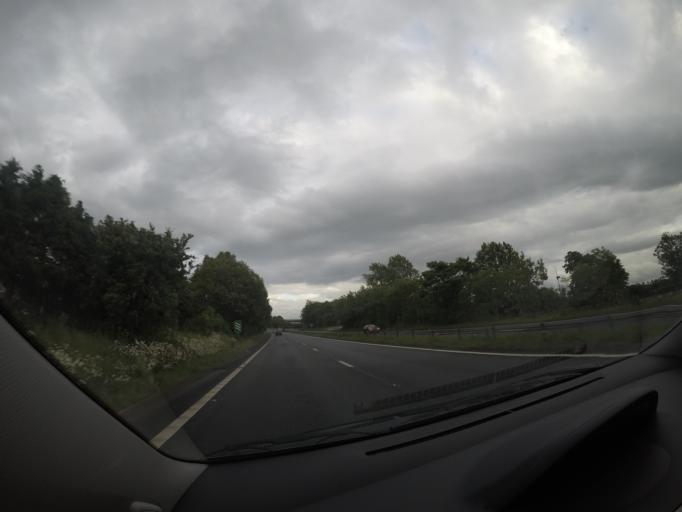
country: GB
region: England
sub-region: Cumbria
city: Kirkby Stephen
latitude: 54.5272
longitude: -2.3272
